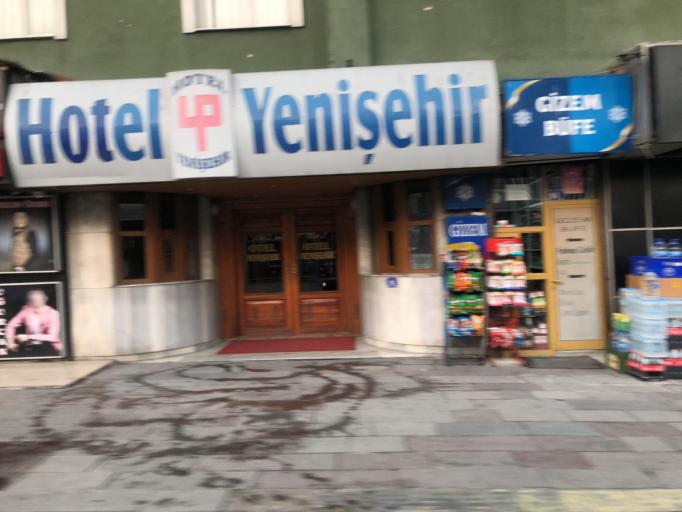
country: TR
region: Ankara
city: Ankara
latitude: 39.9440
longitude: 32.8546
